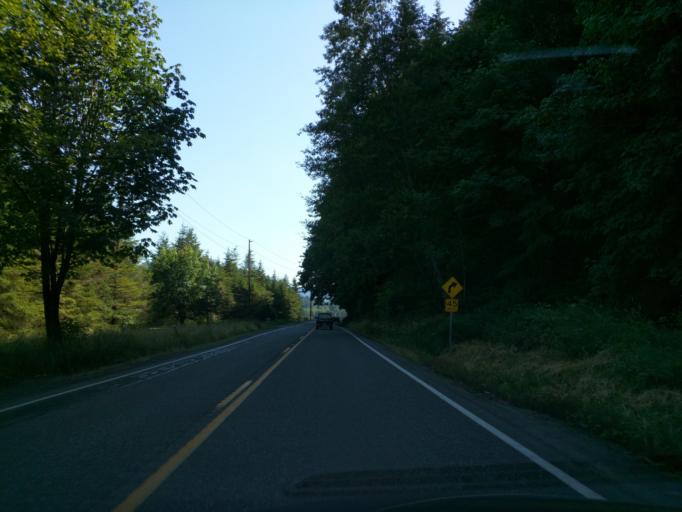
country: US
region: Washington
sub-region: Whatcom County
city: Peaceful Valley
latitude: 48.8547
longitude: -122.1550
